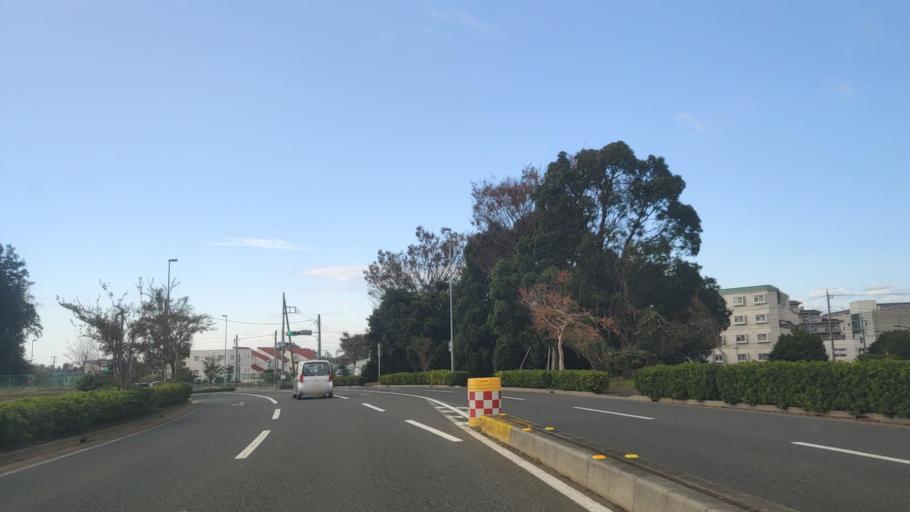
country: JP
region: Kanagawa
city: Minami-rinkan
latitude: 35.4286
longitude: 139.4967
